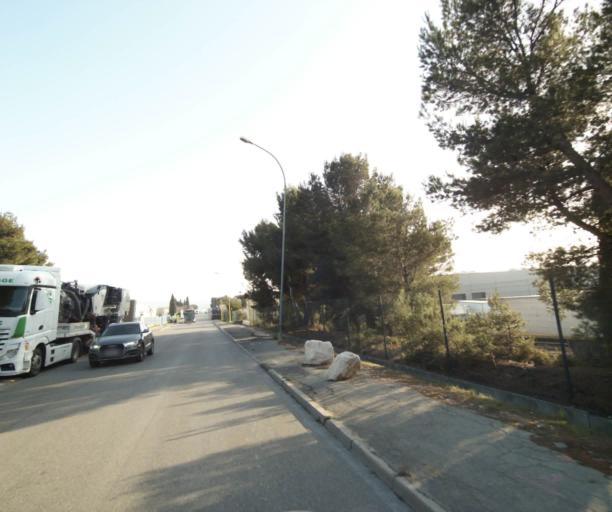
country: FR
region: Provence-Alpes-Cote d'Azur
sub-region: Departement des Bouches-du-Rhone
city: Saint-Victoret
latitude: 43.4381
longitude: 5.2388
